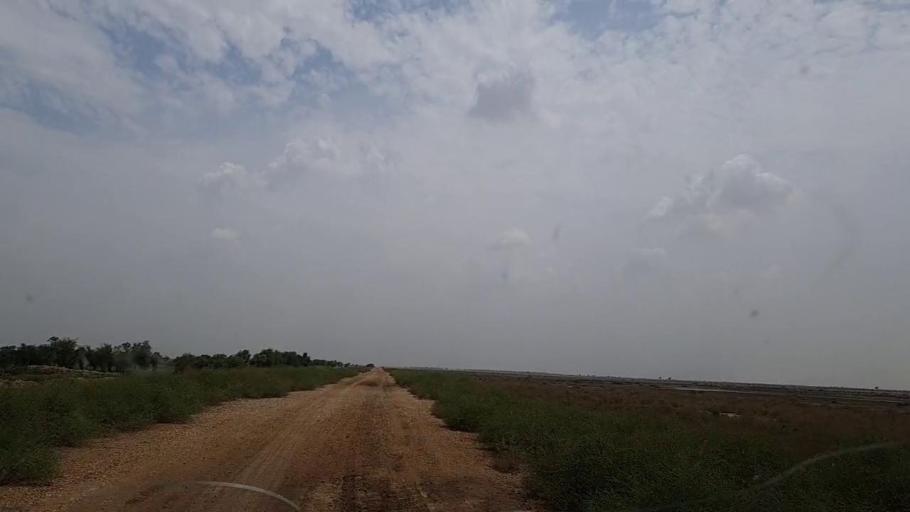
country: PK
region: Sindh
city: Johi
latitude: 26.7922
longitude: 67.6008
